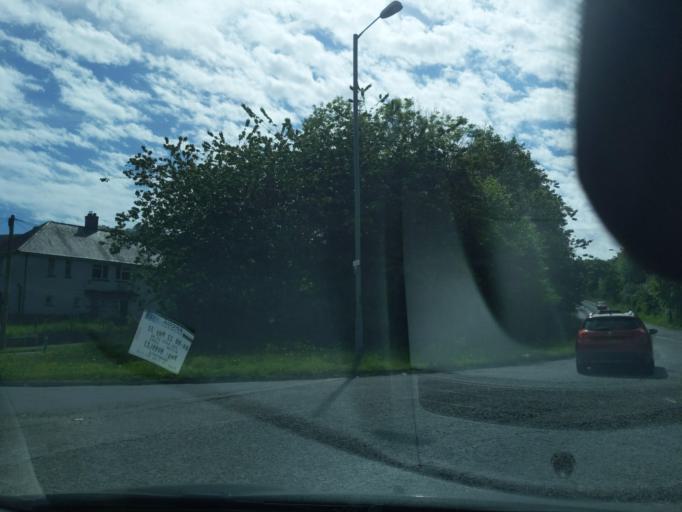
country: GB
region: England
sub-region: Cornwall
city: Penzance
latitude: 50.1291
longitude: -5.5420
